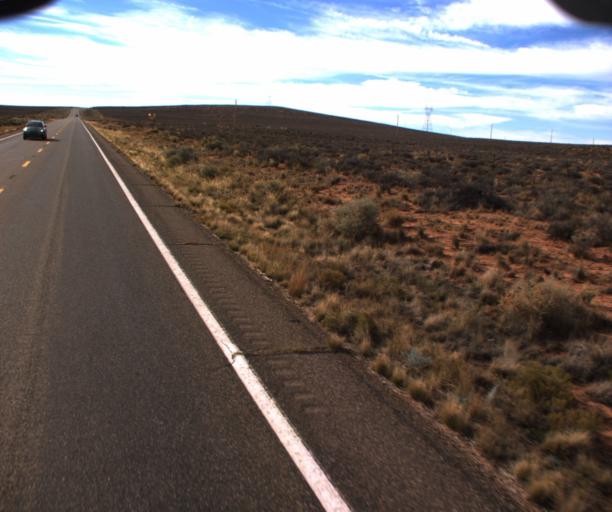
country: US
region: Arizona
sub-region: Coconino County
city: LeChee
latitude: 36.8225
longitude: -111.3084
